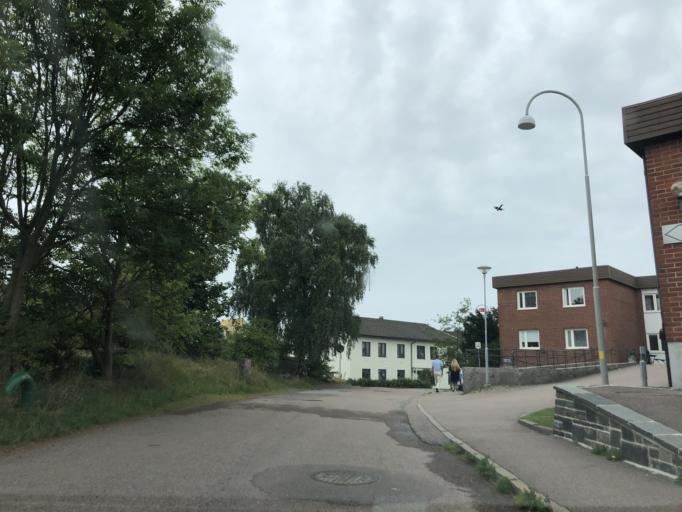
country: SE
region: Vaestra Goetaland
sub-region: Goteborg
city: Majorna
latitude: 57.7117
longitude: 11.9139
